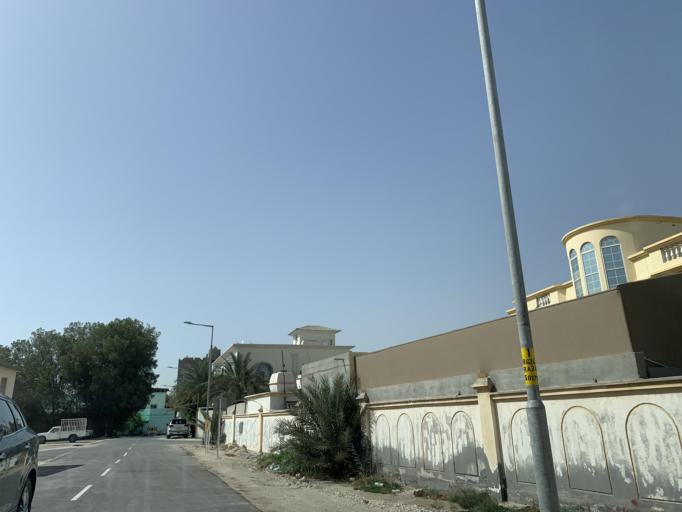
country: BH
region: Northern
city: Sitrah
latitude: 26.1461
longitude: 50.6028
